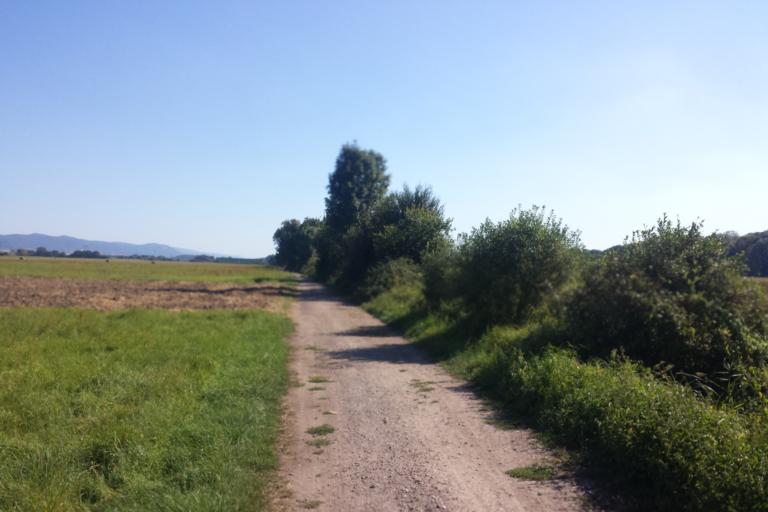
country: DE
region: Hesse
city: Viernheim
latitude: 49.5886
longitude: 8.5961
